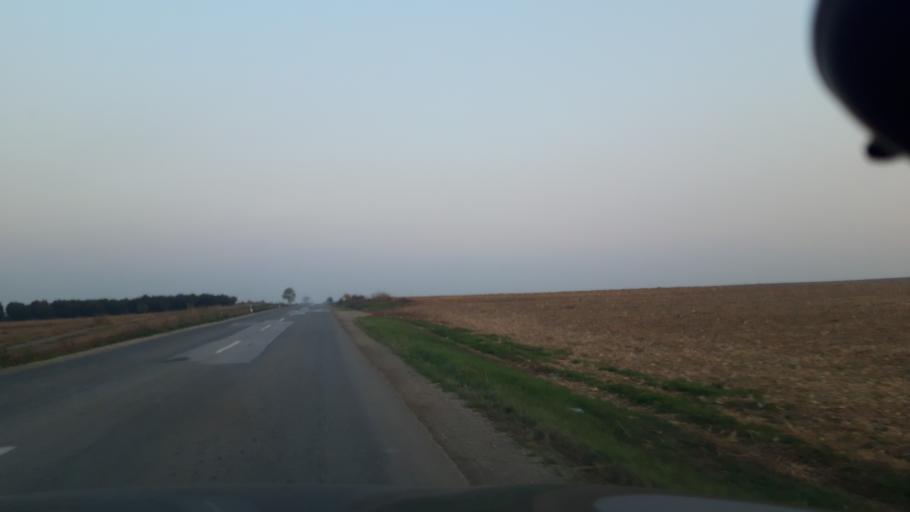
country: RS
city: Putinci
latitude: 44.9991
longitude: 19.9455
